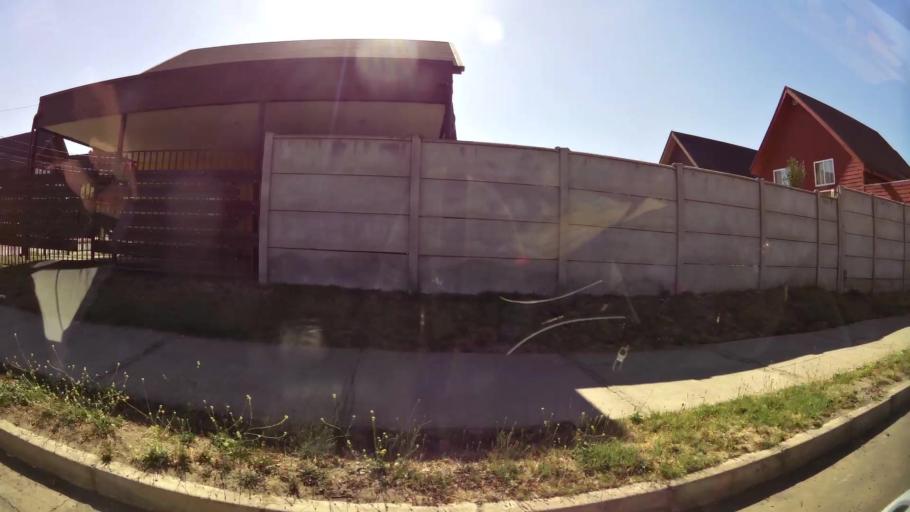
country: CL
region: Maule
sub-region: Provincia de Talca
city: Talca
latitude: -35.4213
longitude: -71.6140
